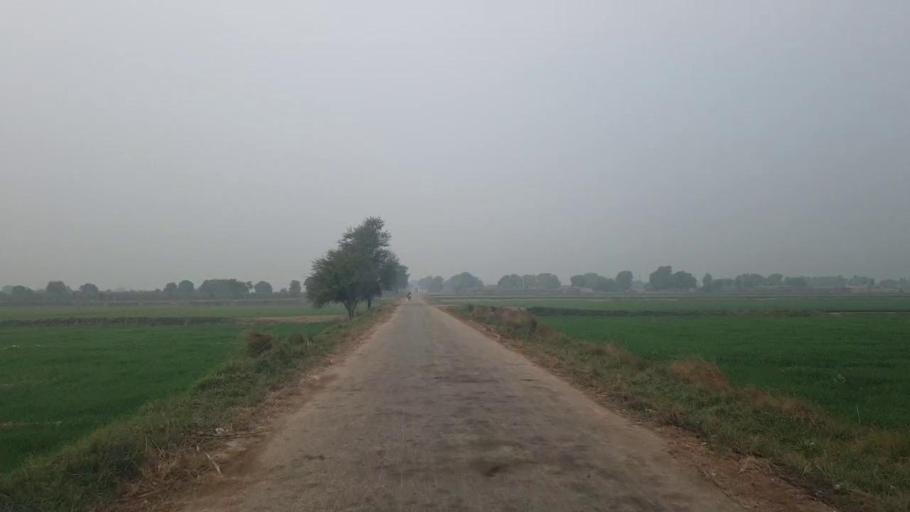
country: PK
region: Sindh
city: Tando Adam
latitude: 25.7098
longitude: 68.6652
